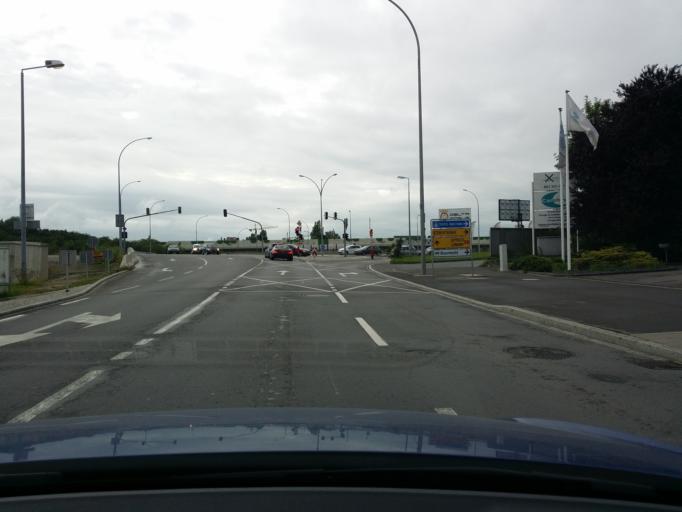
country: LU
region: Luxembourg
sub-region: Canton de Luxembourg
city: Strassen
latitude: 49.6035
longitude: 6.0838
